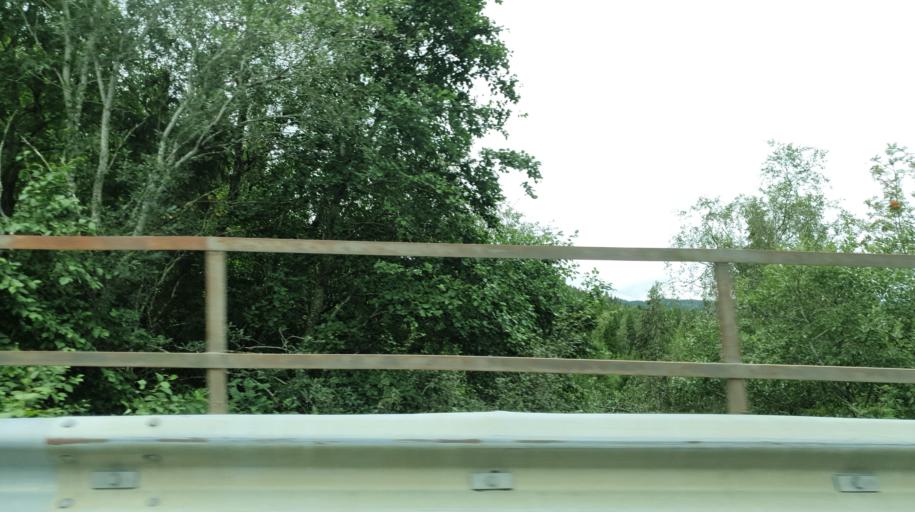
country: NO
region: Nord-Trondelag
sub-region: Stjordal
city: Stjordalshalsen
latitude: 63.4103
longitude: 10.9700
